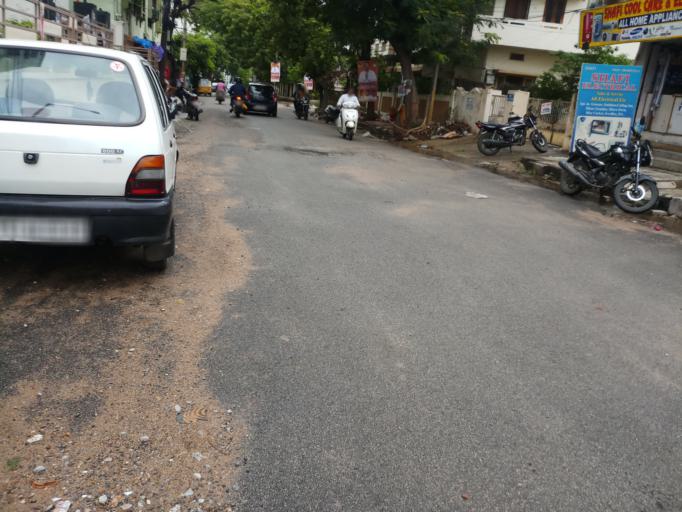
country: IN
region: Telangana
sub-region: Rangareddi
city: Gaddi Annaram
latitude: 17.3672
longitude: 78.5178
